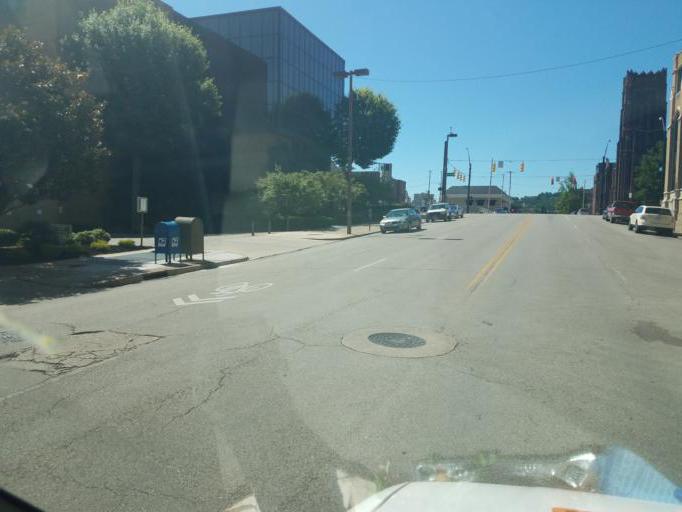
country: US
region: West Virginia
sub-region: Cabell County
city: Huntington
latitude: 38.4204
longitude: -82.4420
